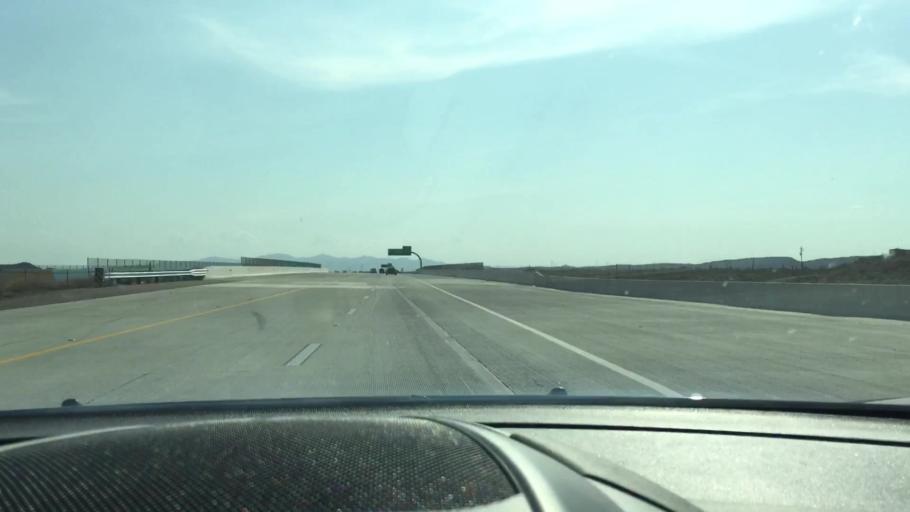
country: US
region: Arizona
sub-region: Maricopa County
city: Anthem
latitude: 33.7787
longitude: -112.2275
